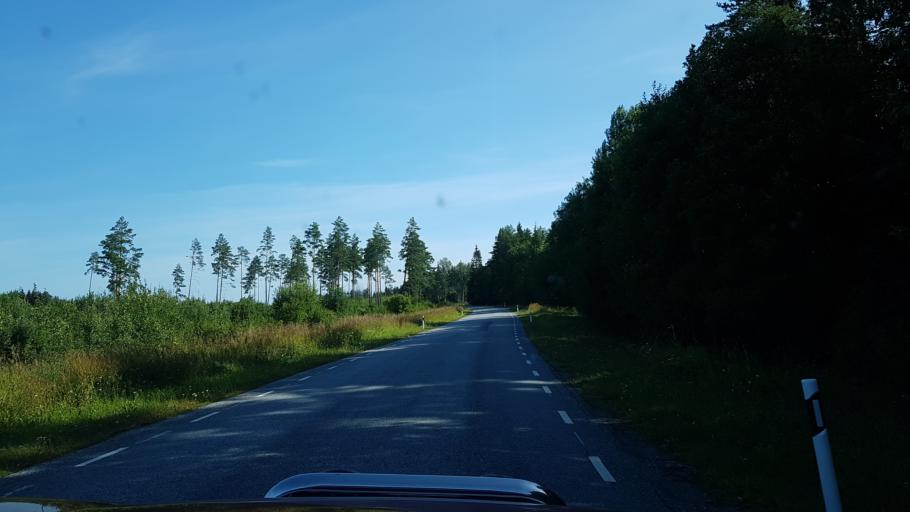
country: EE
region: Harju
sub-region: Raasiku vald
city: Raasiku
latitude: 59.2878
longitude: 25.1645
